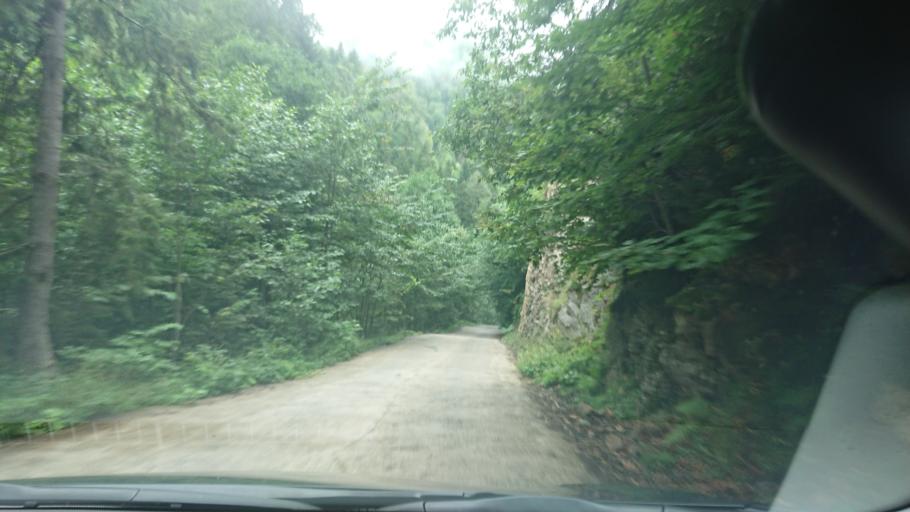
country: TR
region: Gumushane
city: Kurtun
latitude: 40.6678
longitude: 39.0394
